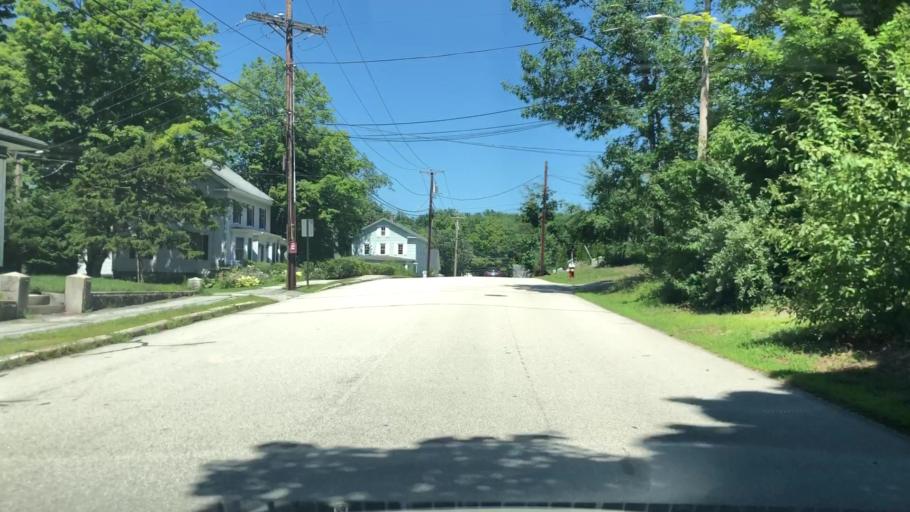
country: US
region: New Hampshire
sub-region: Hillsborough County
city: Milford
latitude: 42.8363
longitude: -71.6445
